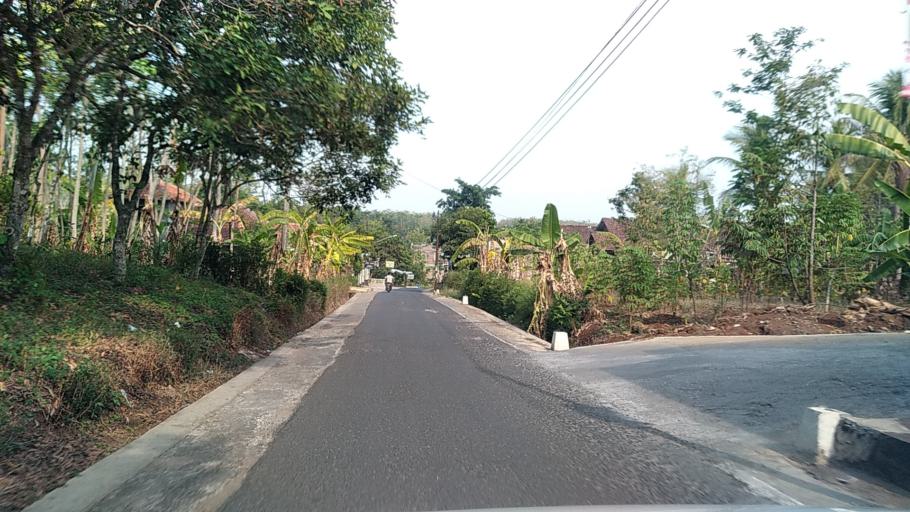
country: ID
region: Central Java
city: Semarang
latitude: -7.0393
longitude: 110.3009
